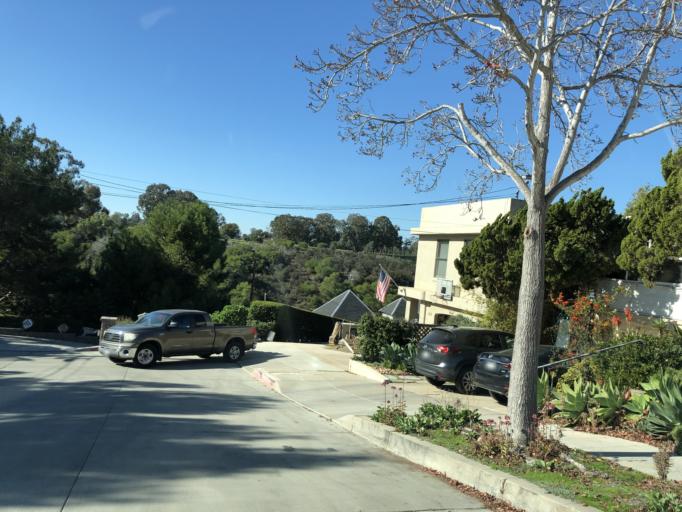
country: US
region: California
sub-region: San Diego County
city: San Diego
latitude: 32.7297
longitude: -117.1331
